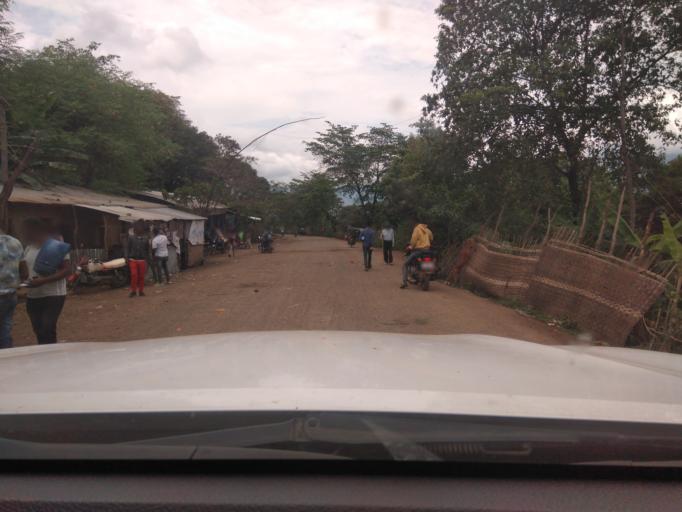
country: ET
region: Southern Nations, Nationalities, and People's Region
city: Felege Neway
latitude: 6.3973
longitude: 37.0844
